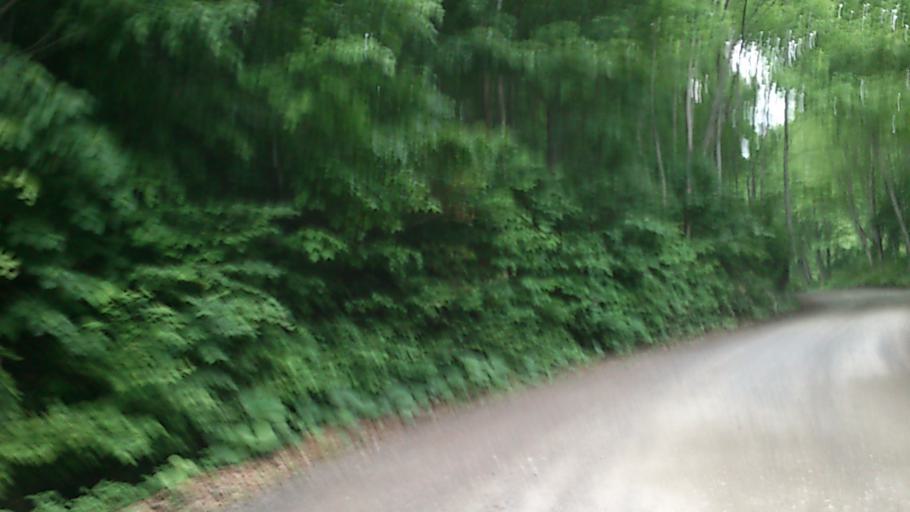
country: JP
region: Aomori
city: Hirosaki
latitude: 40.5626
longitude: 140.1731
